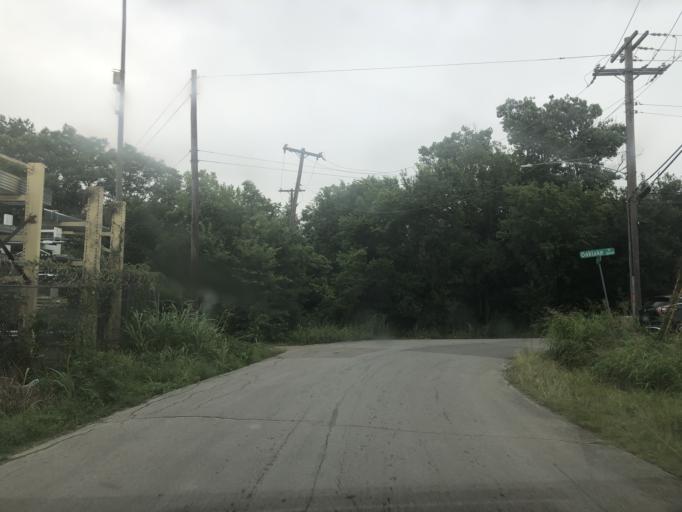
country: US
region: Texas
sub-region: Dallas County
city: Farmers Branch
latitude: 32.8637
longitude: -96.8760
